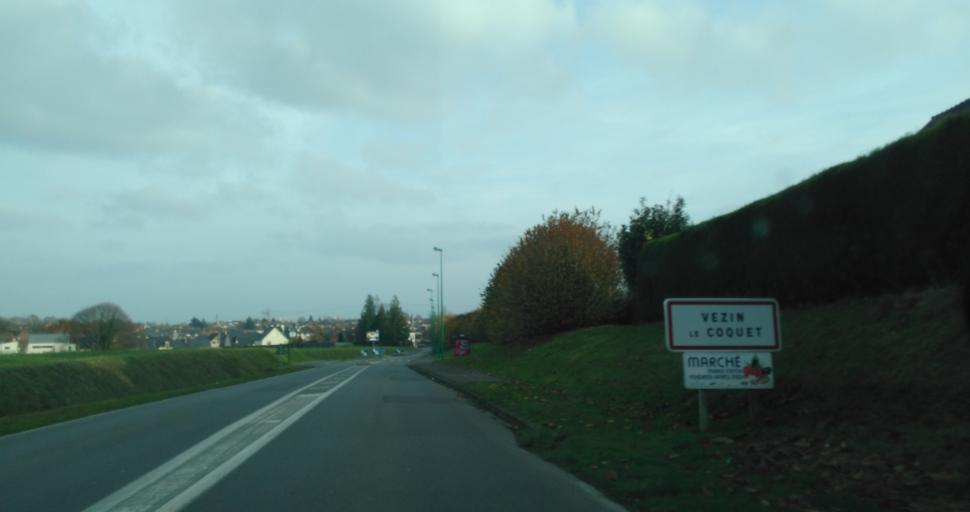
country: FR
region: Brittany
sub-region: Departement d'Ille-et-Vilaine
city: Vezin-le-Coquet
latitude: 48.1205
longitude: -1.7667
